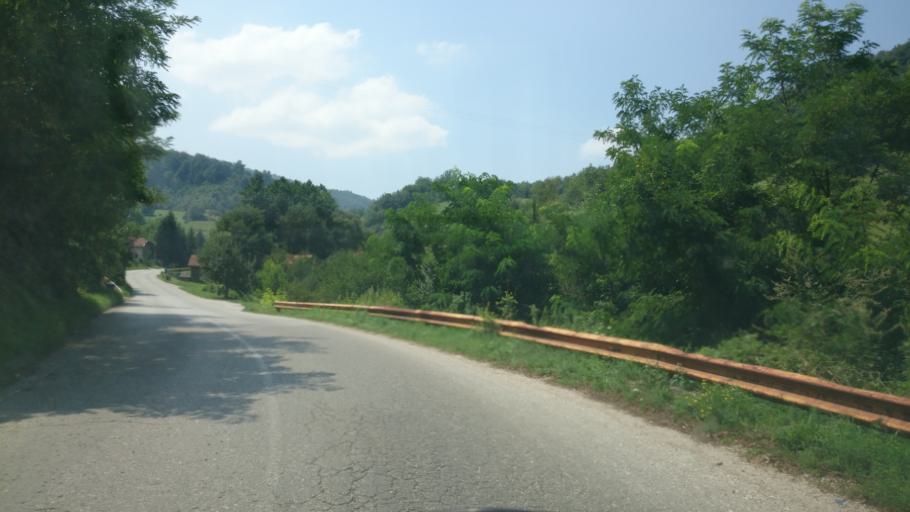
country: BA
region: Federation of Bosnia and Herzegovina
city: Lokvine
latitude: 44.1943
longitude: 17.8751
